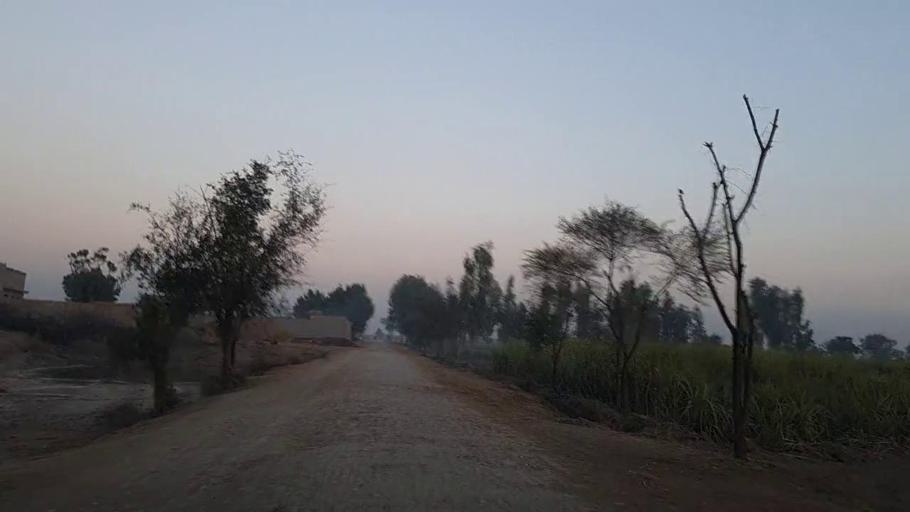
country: PK
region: Sindh
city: Naushahro Firoz
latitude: 26.7900
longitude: 68.0443
